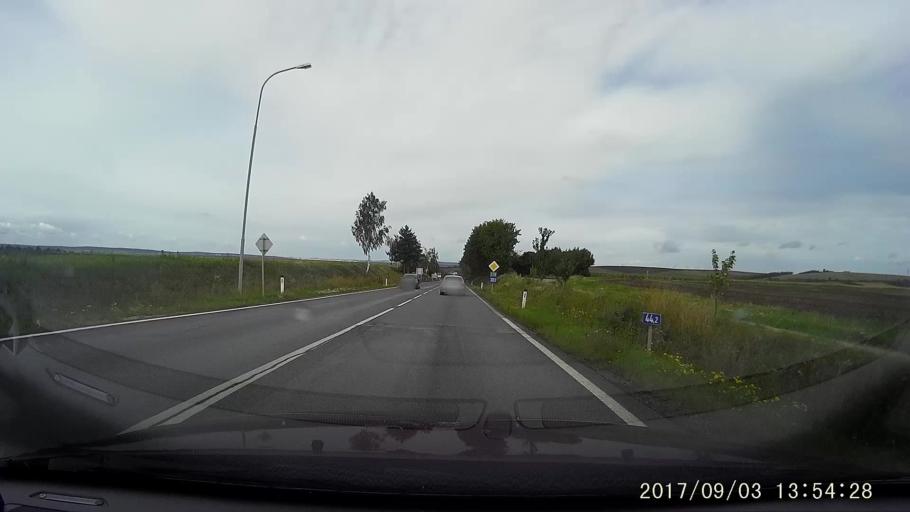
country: AT
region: Lower Austria
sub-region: Politischer Bezirk Hollabrunn
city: Haugsdorf
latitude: 48.7422
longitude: 16.0603
